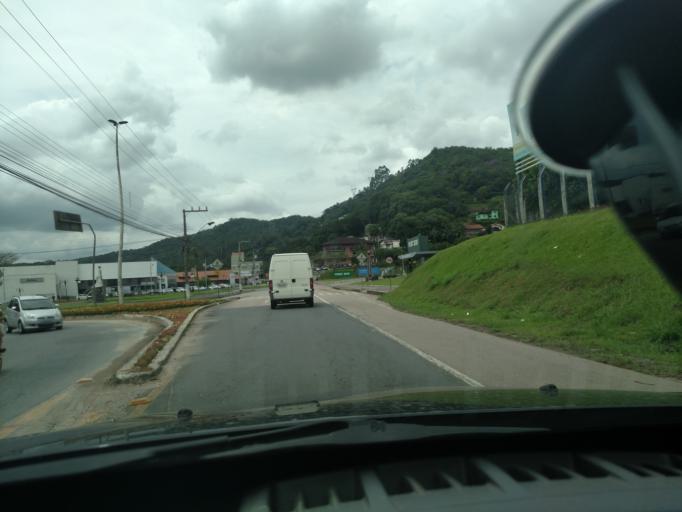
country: BR
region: Santa Catarina
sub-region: Blumenau
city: Blumenau
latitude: -26.9072
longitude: -49.0346
